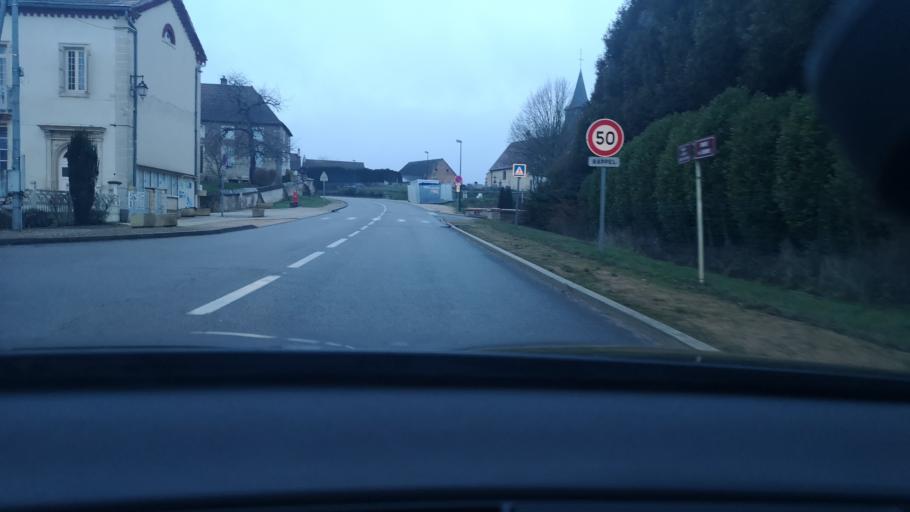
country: FR
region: Bourgogne
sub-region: Departement de la Cote-d'Or
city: Seurre
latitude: 47.0590
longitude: 5.0762
